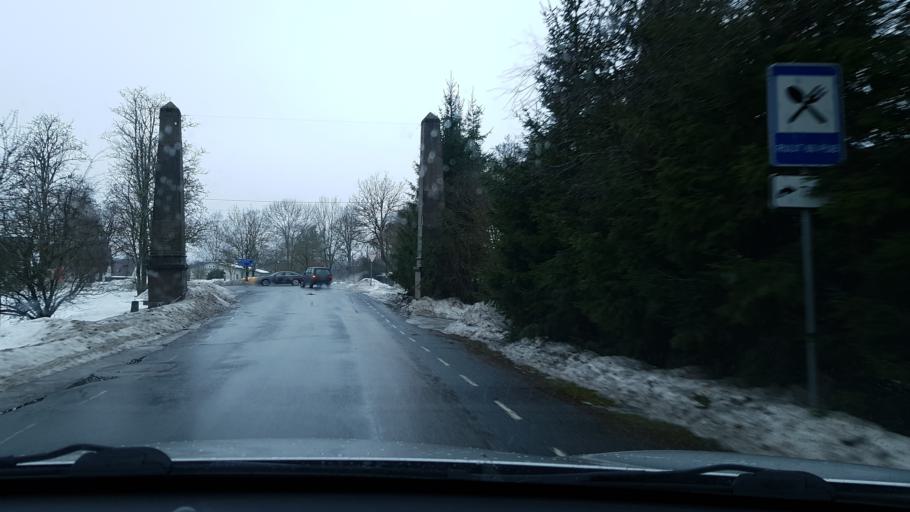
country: EE
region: Raplamaa
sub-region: Maerjamaa vald
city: Marjamaa
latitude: 58.9018
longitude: 24.4242
